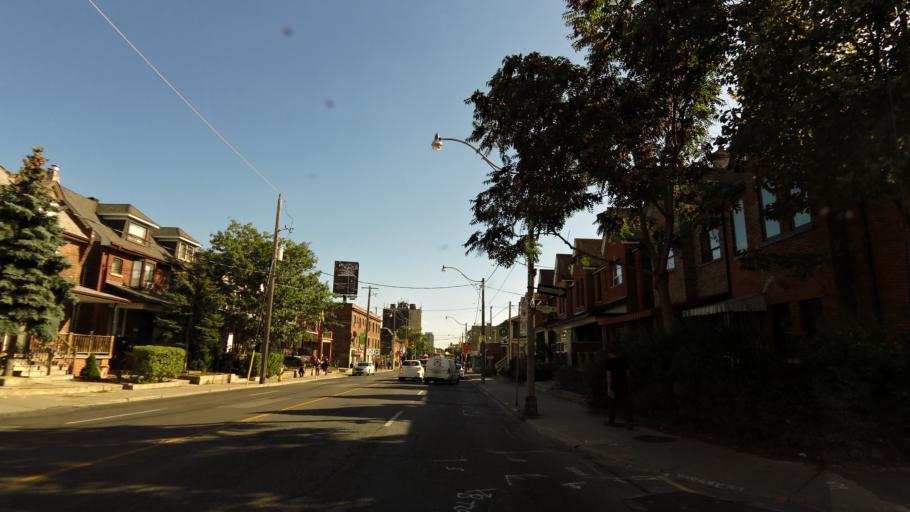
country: CA
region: Ontario
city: Toronto
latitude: 43.6535
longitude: -79.4330
